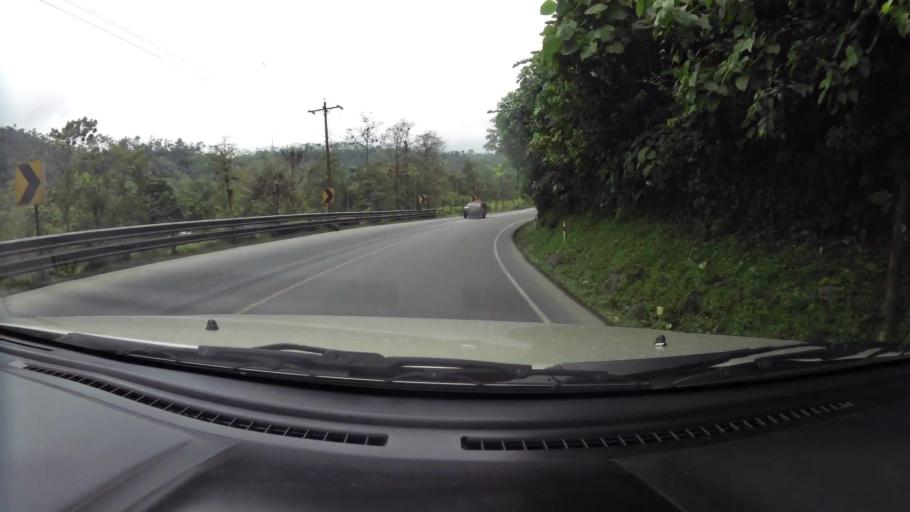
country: EC
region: Santo Domingo de los Tsachilas
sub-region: Canton Santo Domingo de los Colorados
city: Santo Domingo de los Colorados
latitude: -0.2675
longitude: -79.0882
